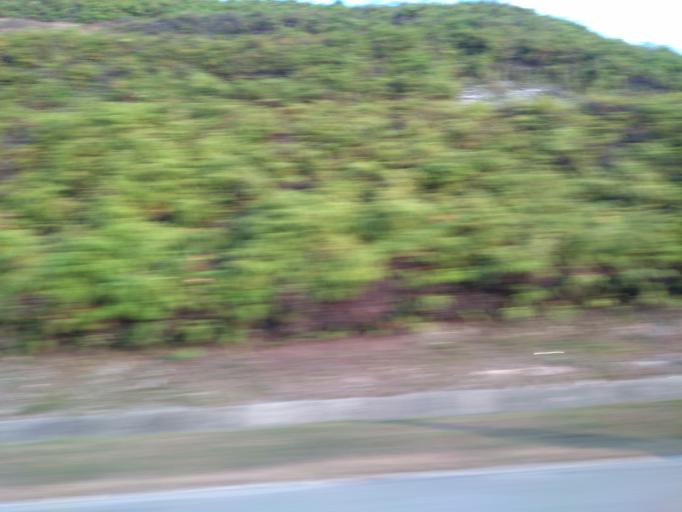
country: MY
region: Putrajaya
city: Putrajaya
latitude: 2.9715
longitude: 101.6685
